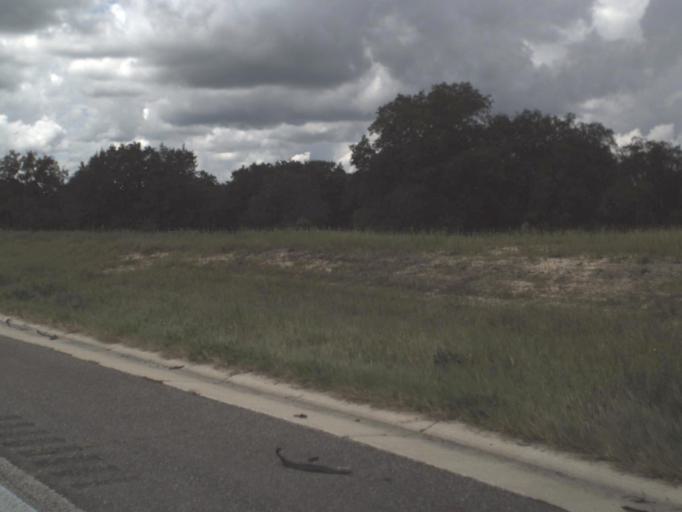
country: US
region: Florida
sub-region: Polk County
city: Loughman
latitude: 28.2465
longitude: -81.6314
